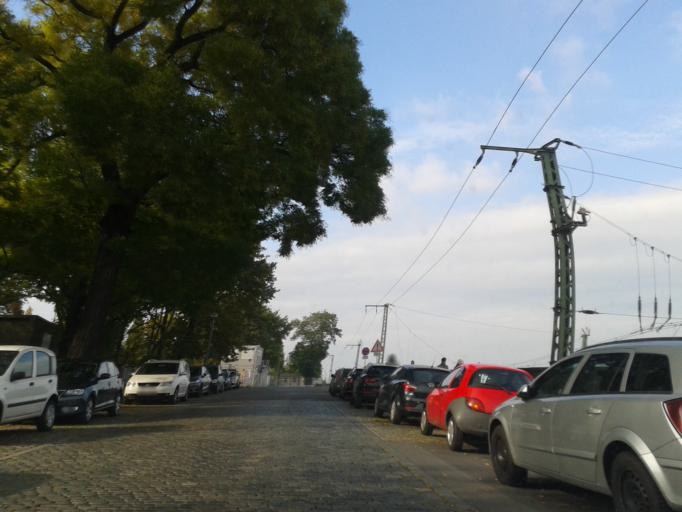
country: DE
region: Saxony
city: Dresden
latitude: 51.0412
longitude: 13.7272
